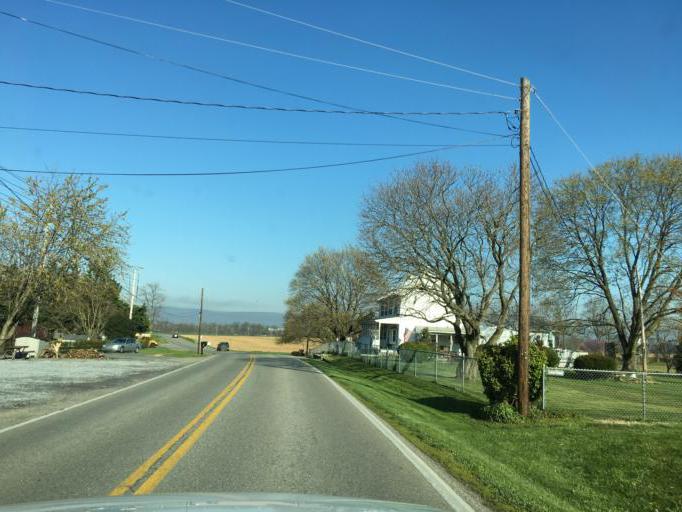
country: US
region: Maryland
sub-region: Frederick County
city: Walkersville
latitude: 39.4942
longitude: -77.3338
